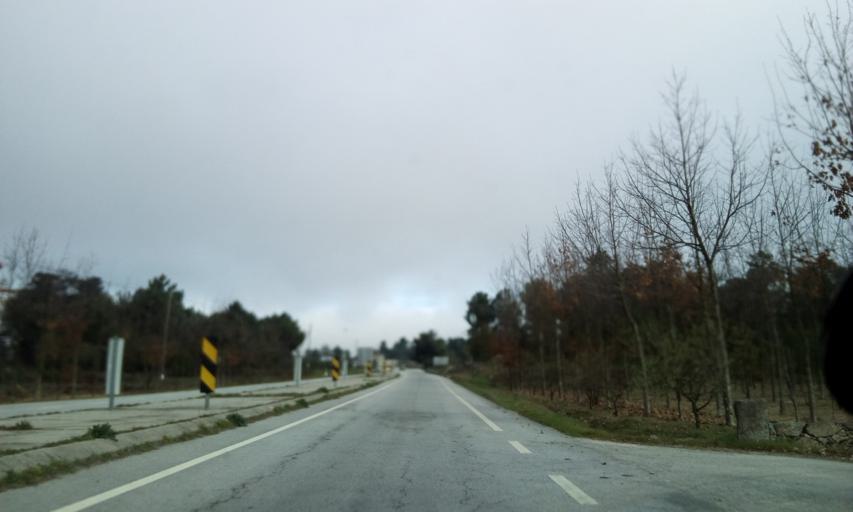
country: PT
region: Guarda
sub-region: Aguiar da Beira
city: Aguiar da Beira
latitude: 40.7359
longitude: -7.4935
